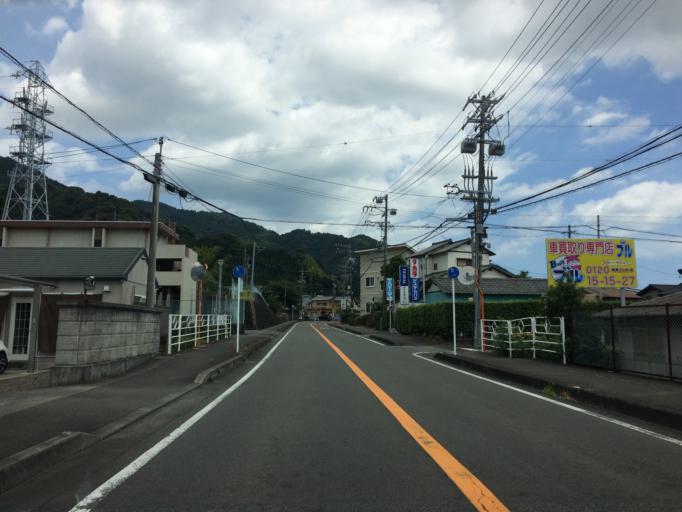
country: JP
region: Shizuoka
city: Fujieda
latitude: 34.9058
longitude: 138.2890
